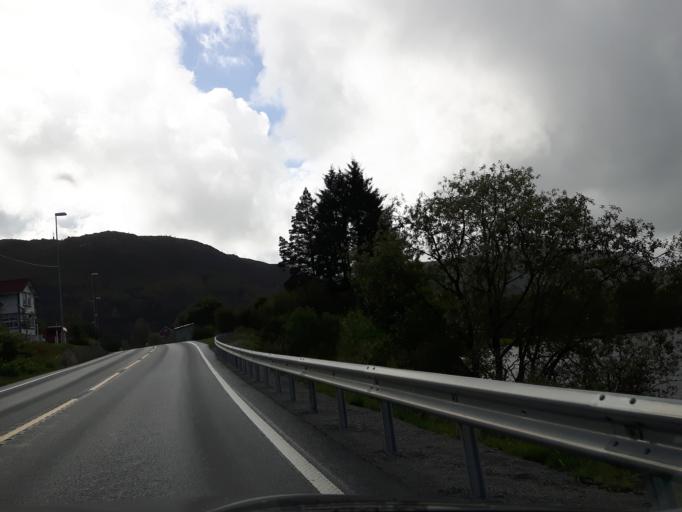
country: NO
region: Rogaland
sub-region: Sokndal
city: Hauge i Dalane
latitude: 58.4695
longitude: 6.3651
